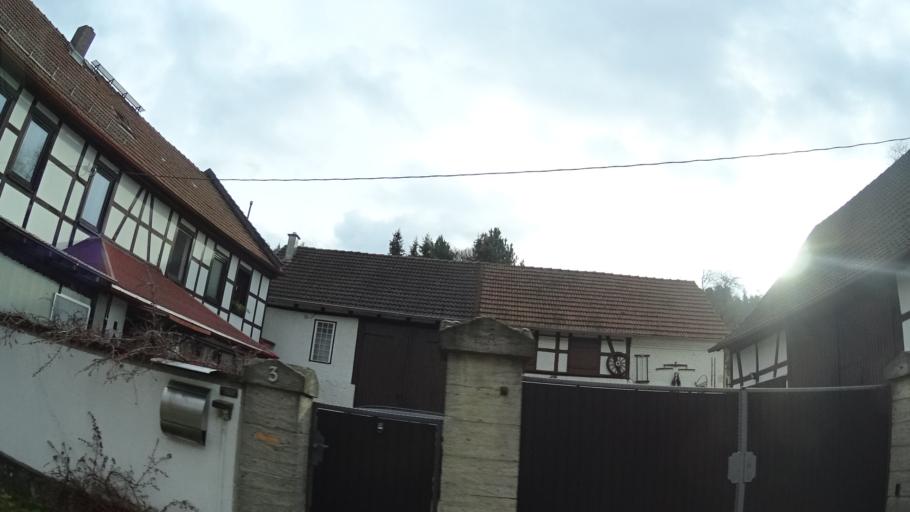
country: DE
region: Thuringia
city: Reinstadt
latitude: 50.7867
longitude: 11.4797
